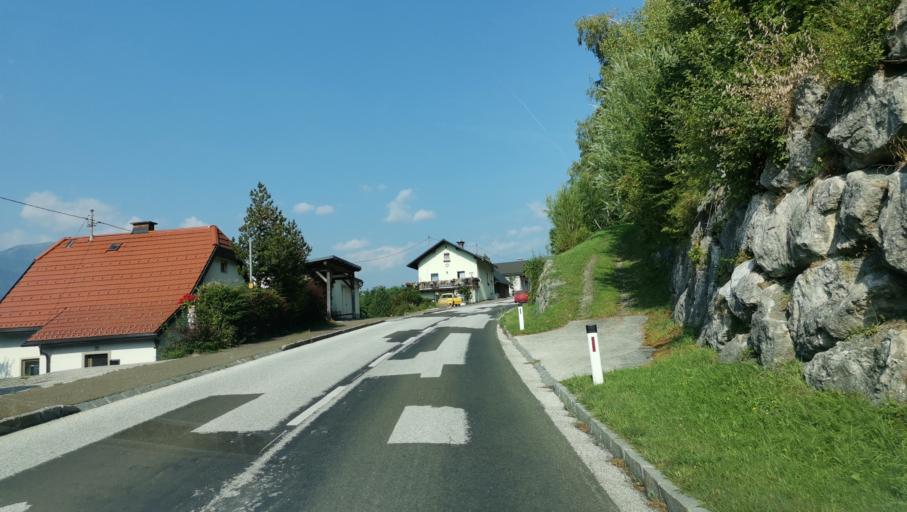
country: AT
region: Styria
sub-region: Politischer Bezirk Liezen
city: Trieben
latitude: 47.5050
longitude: 14.4750
